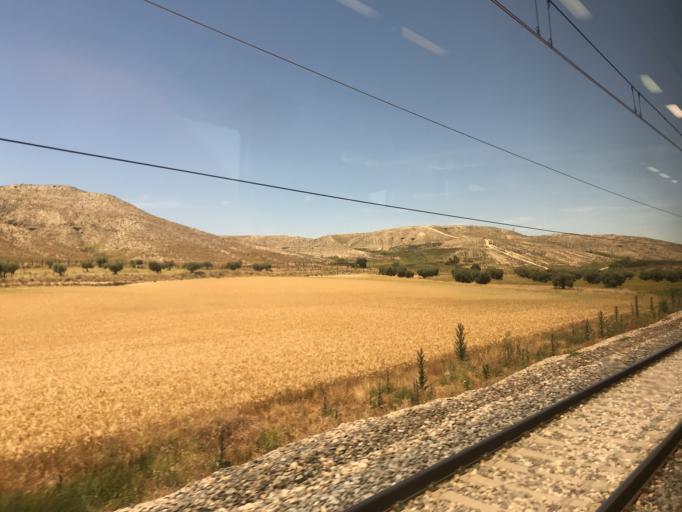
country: ES
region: Madrid
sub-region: Provincia de Madrid
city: Ciempozuelos
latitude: 40.1348
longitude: -3.6134
